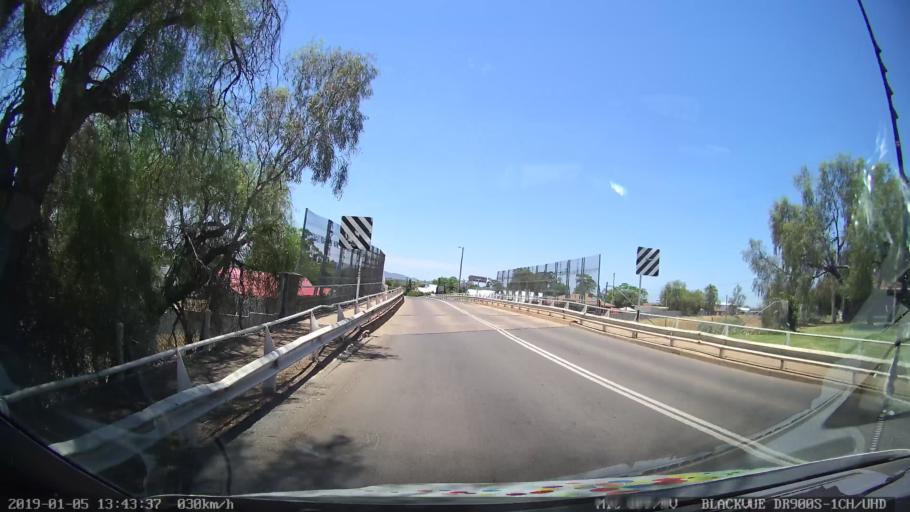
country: AU
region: New South Wales
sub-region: Gunnedah
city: Gunnedah
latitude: -30.9820
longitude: 150.2534
